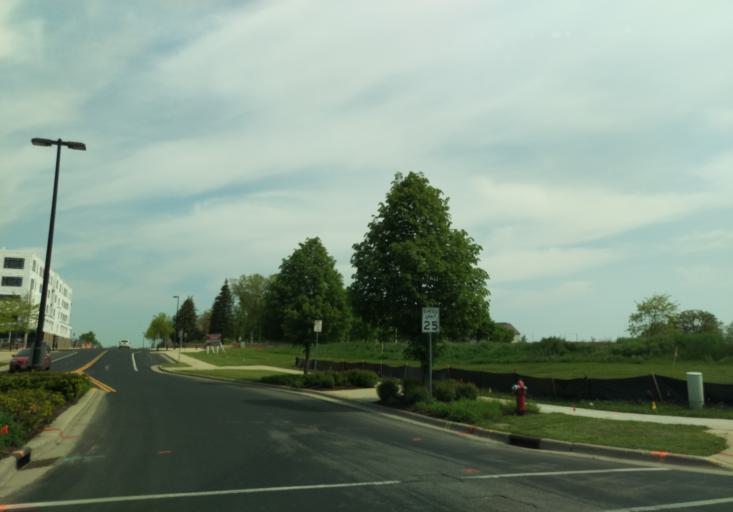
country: US
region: Wisconsin
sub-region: Dane County
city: Monona
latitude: 43.0847
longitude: -89.2796
